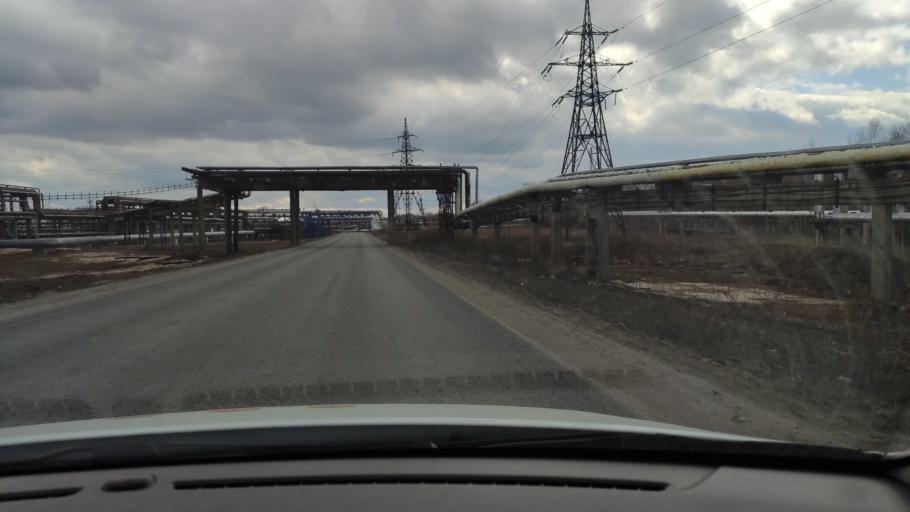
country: RU
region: Tatarstan
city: Staroye Arakchino
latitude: 55.8722
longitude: 48.9743
